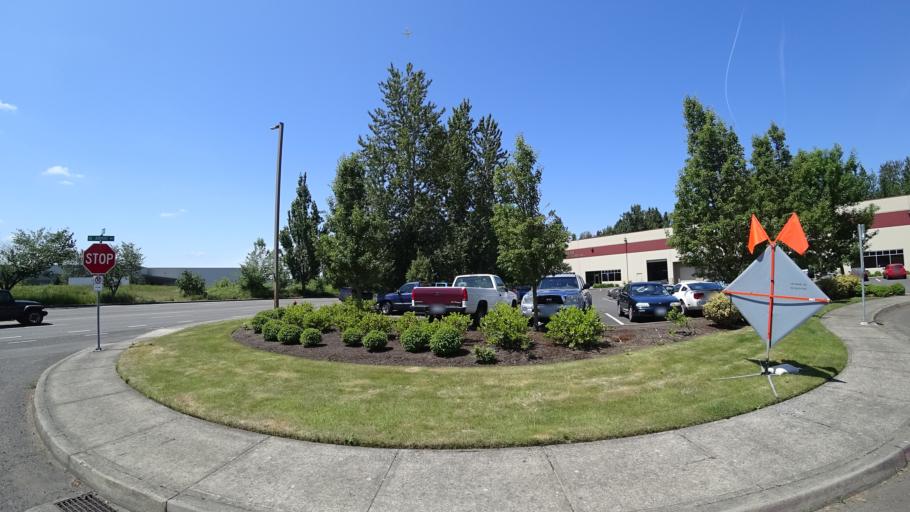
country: US
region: Oregon
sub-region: Multnomah County
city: Fairview
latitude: 45.5540
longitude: -122.4894
